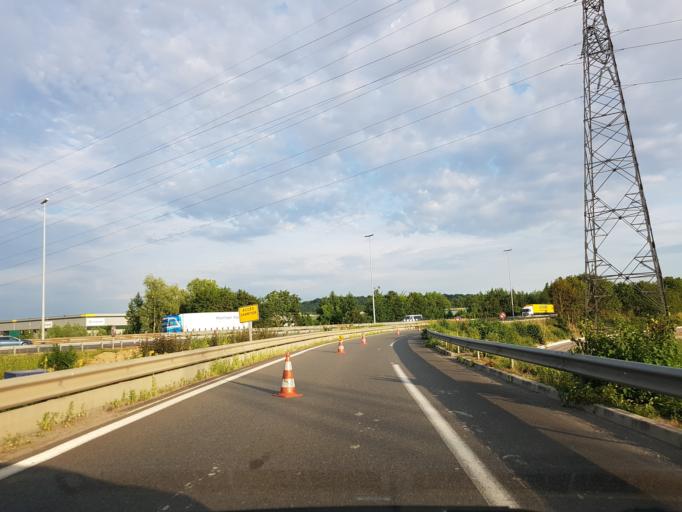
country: FR
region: Picardie
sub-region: Departement de l'Oise
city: Chevrieres
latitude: 49.3189
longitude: 2.6857
